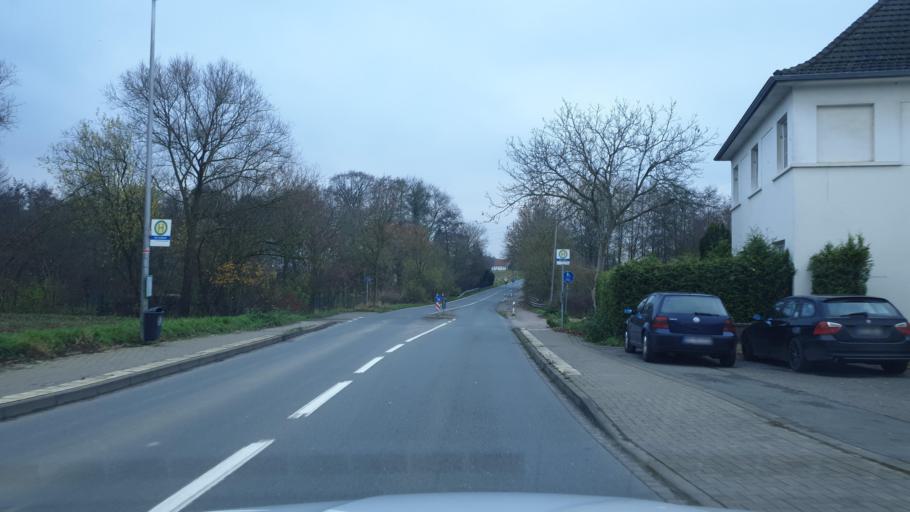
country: DE
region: North Rhine-Westphalia
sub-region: Regierungsbezirk Detmold
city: Hiddenhausen
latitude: 52.1235
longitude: 8.6138
